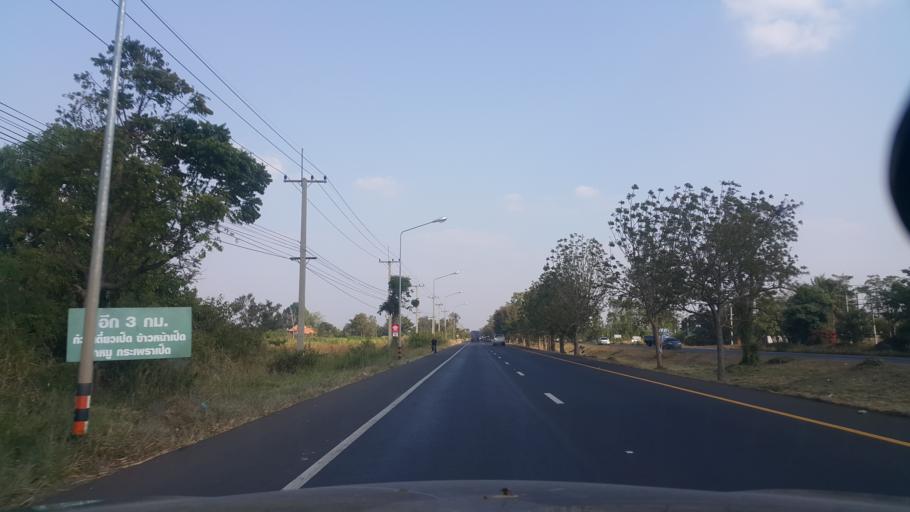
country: TH
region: Buriram
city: Nong Ki
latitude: 14.6639
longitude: 102.6119
